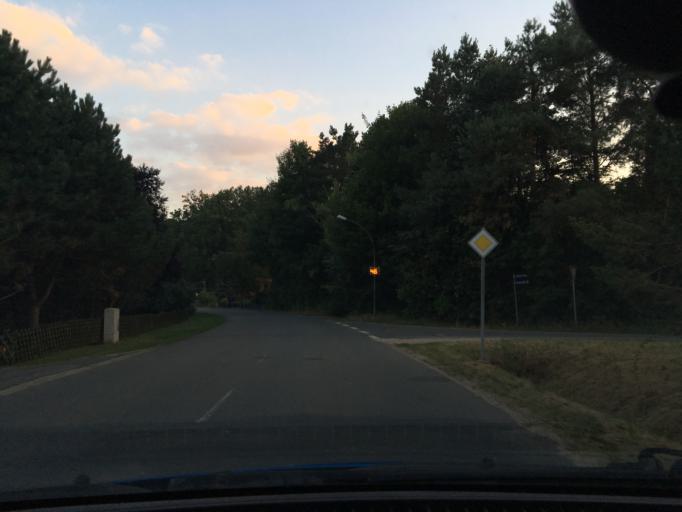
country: DE
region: Lower Saxony
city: Natendorf
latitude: 53.1099
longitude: 10.4555
